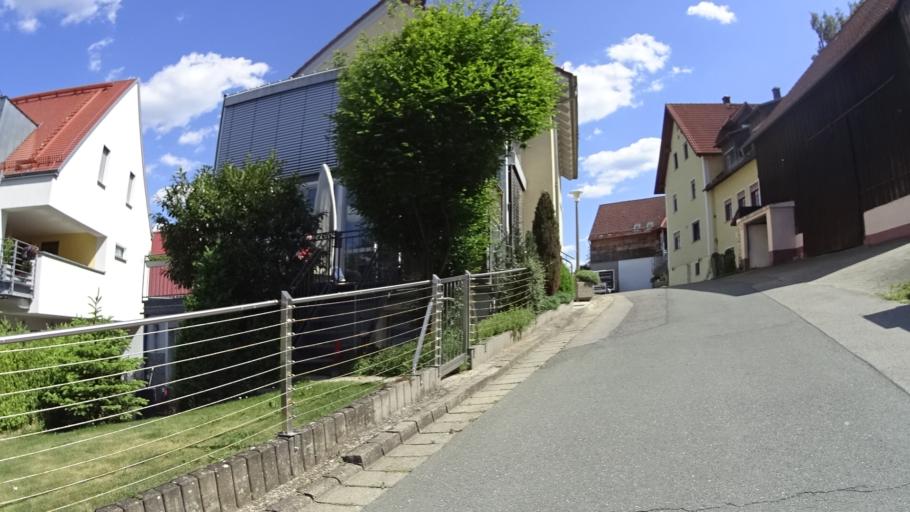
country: DE
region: Bavaria
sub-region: Regierungsbezirk Mittelfranken
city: Greding
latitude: 49.0607
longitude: 11.3199
